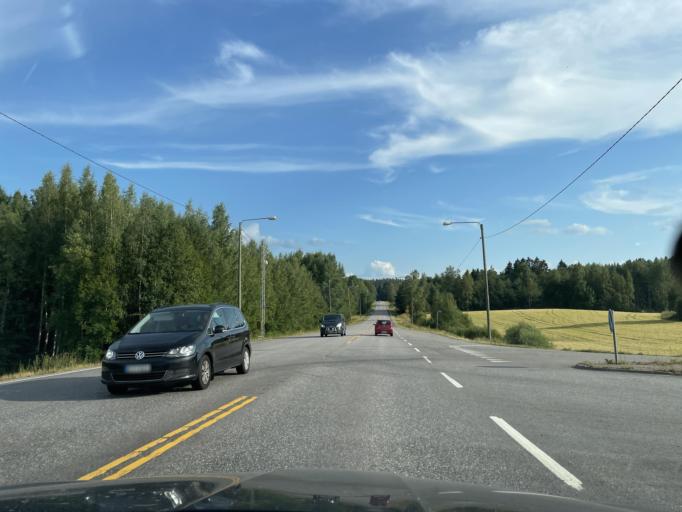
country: FI
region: Paijanne Tavastia
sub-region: Lahti
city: Padasjoki
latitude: 61.3907
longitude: 25.1883
